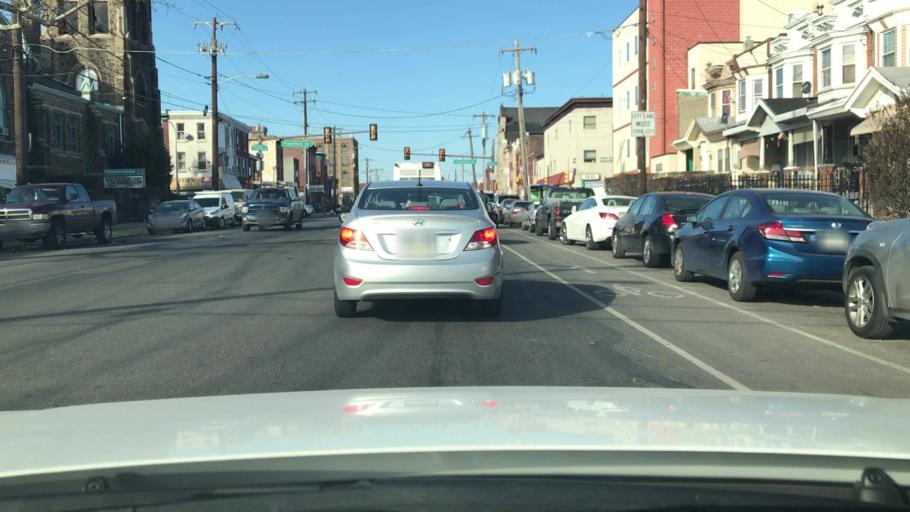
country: US
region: New Jersey
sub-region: Camden County
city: Merchantville
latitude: 39.9924
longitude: -75.1097
